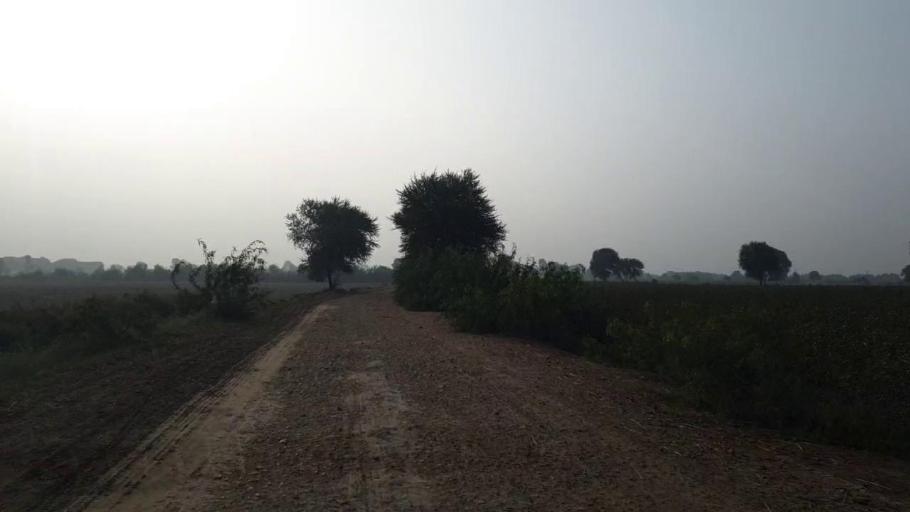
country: PK
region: Sindh
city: Tando Muhammad Khan
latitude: 25.1810
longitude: 68.6009
